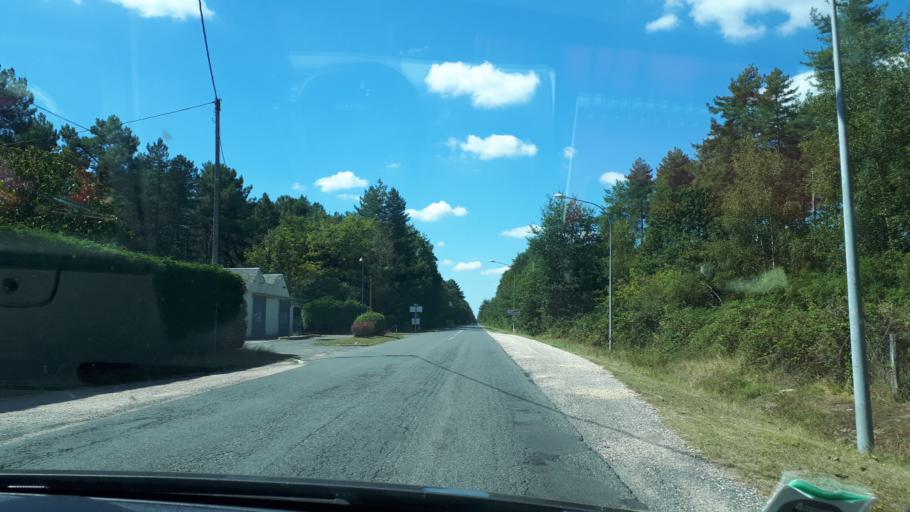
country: FR
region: Centre
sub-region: Departement du Loir-et-Cher
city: Neung-sur-Beuvron
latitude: 47.5397
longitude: 1.8447
